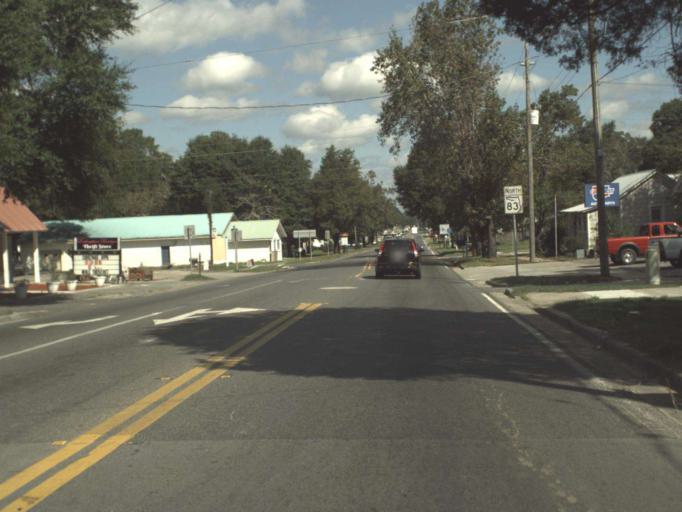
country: US
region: Florida
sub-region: Walton County
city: DeFuniak Springs
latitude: 30.7216
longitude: -86.1153
